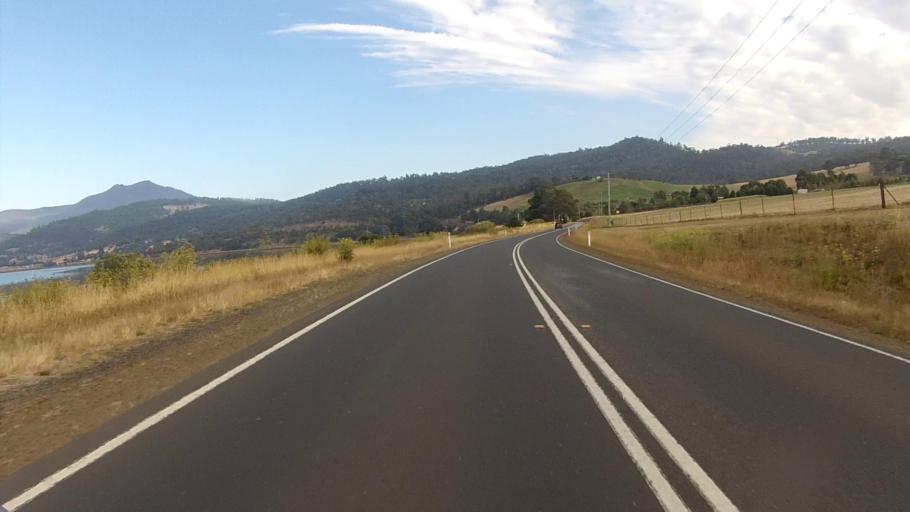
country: AU
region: Tasmania
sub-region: Brighton
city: Bridgewater
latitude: -42.7294
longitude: 147.2067
